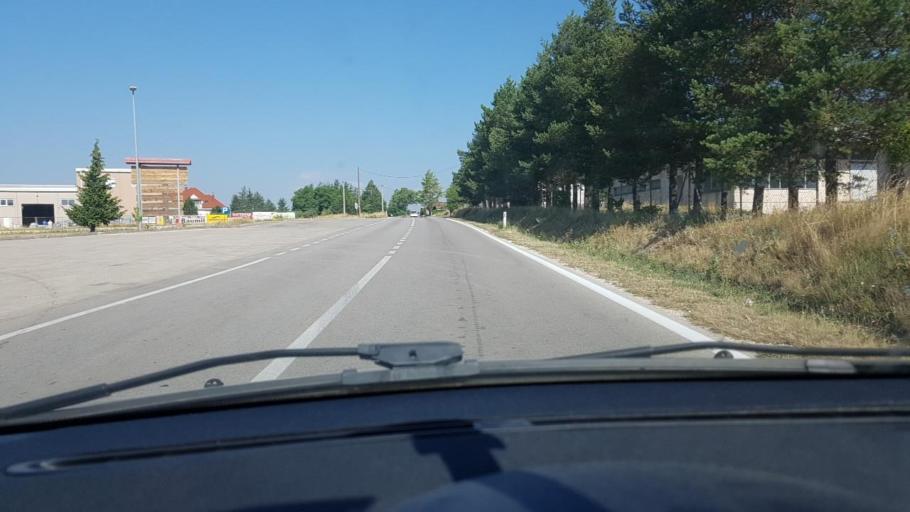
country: BA
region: Federation of Bosnia and Herzegovina
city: Livno
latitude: 43.8428
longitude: 16.9682
